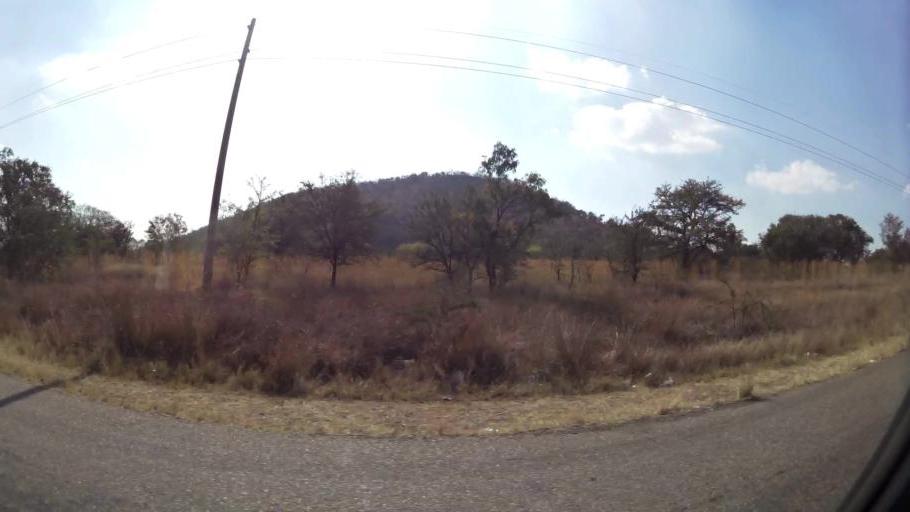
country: ZA
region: North-West
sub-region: Bojanala Platinum District Municipality
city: Rustenburg
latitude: -25.6320
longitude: 27.1787
